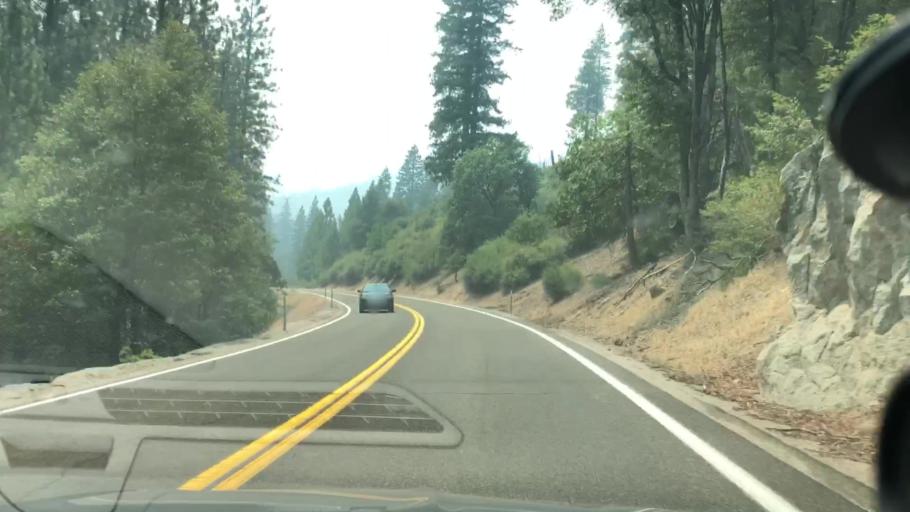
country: US
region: California
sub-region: El Dorado County
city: Pollock Pines
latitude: 38.7764
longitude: -120.2816
